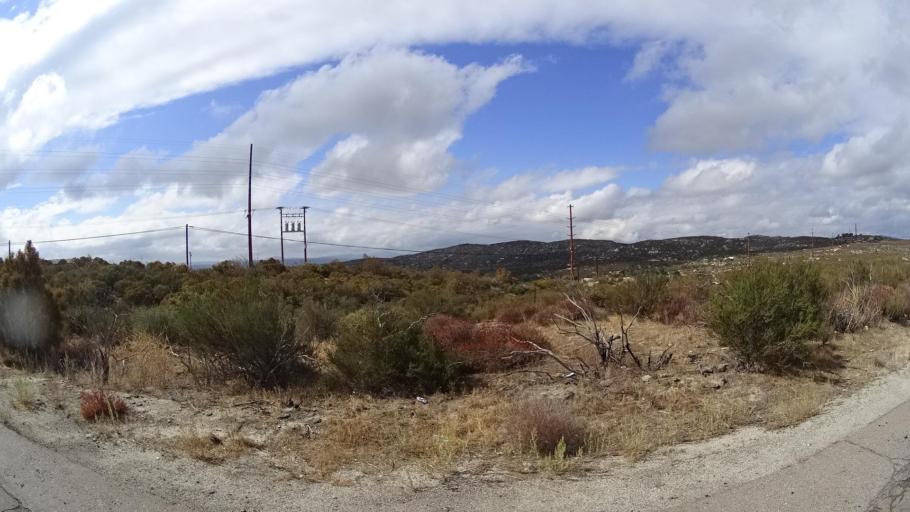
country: US
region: California
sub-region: San Diego County
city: Campo
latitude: 32.6996
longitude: -116.3559
